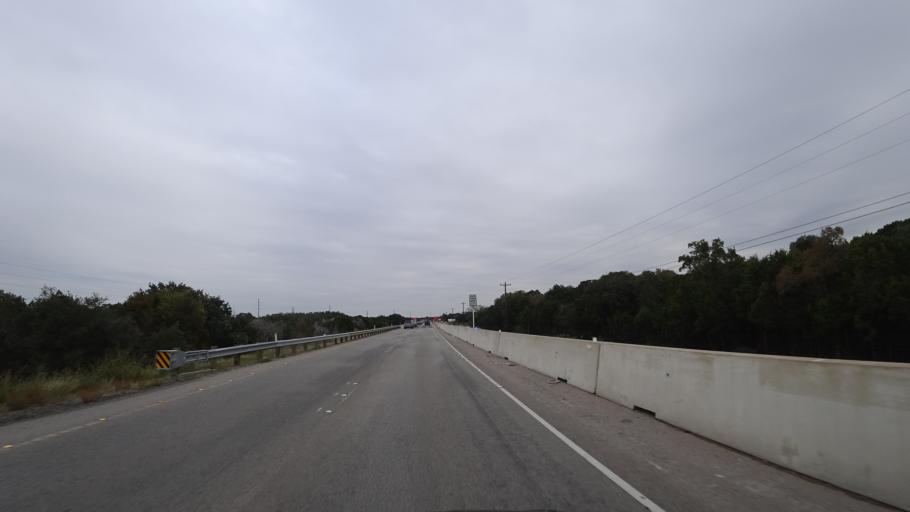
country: US
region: Texas
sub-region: Travis County
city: Shady Hollow
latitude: 30.1781
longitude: -97.8950
